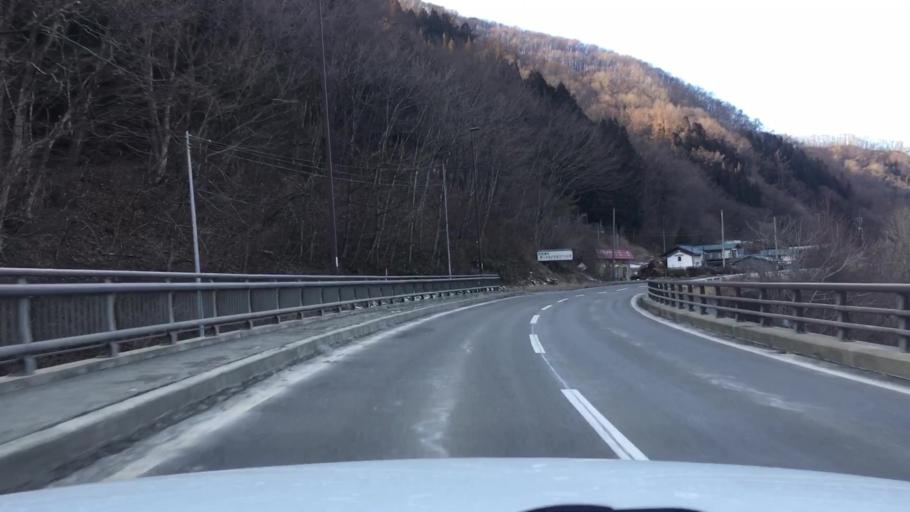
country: JP
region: Iwate
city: Tono
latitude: 39.6154
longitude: 141.6259
